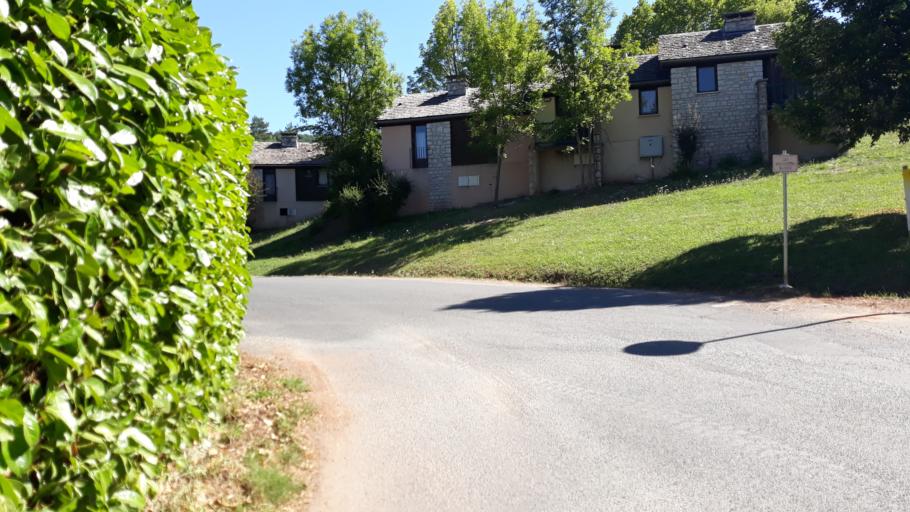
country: FR
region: Languedoc-Roussillon
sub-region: Departement de la Lozere
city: La Canourgue
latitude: 44.4366
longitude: 3.2033
